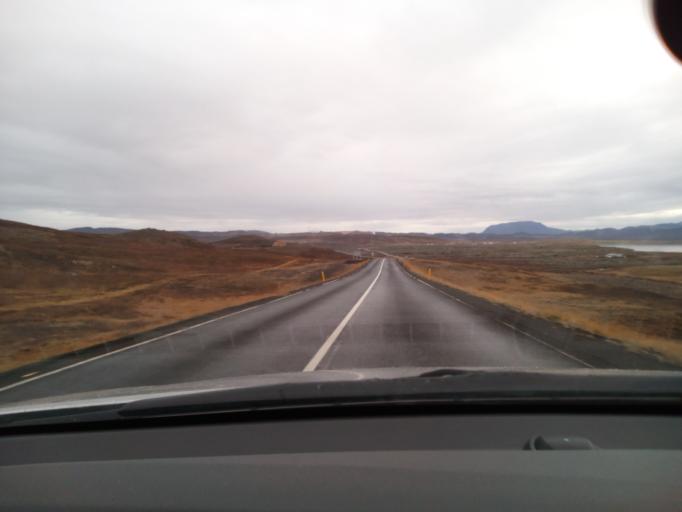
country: IS
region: Northeast
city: Laugar
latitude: 65.6604
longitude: -16.9743
